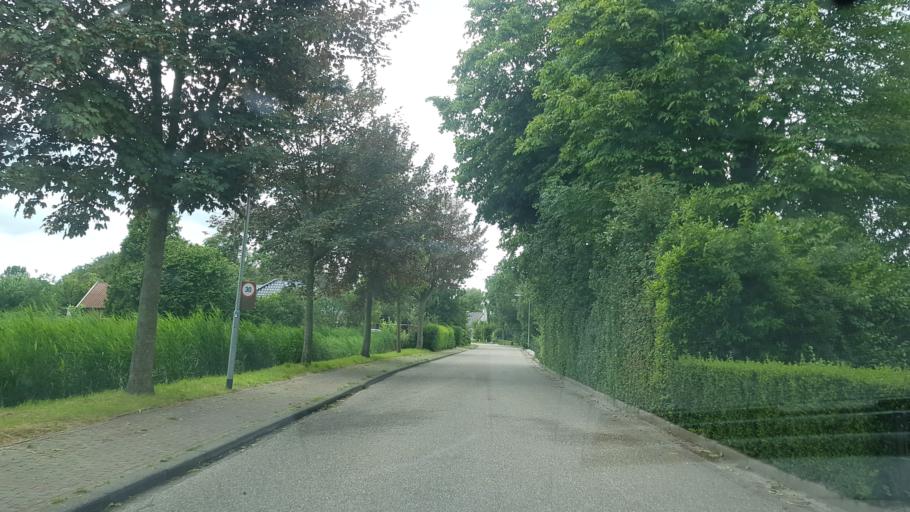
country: NL
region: Groningen
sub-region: Gemeente Winsum
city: Winsum
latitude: 53.4000
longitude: 6.4871
